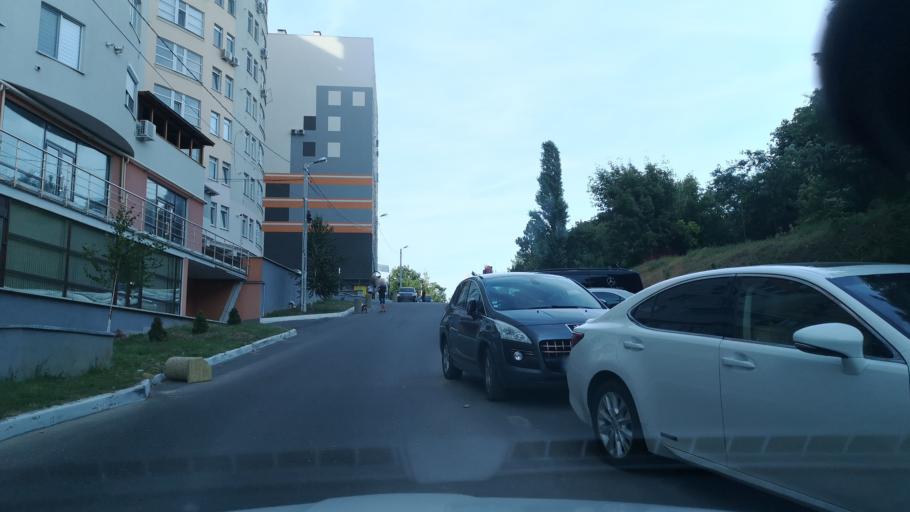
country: MD
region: Chisinau
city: Chisinau
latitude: 47.0025
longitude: 28.8449
